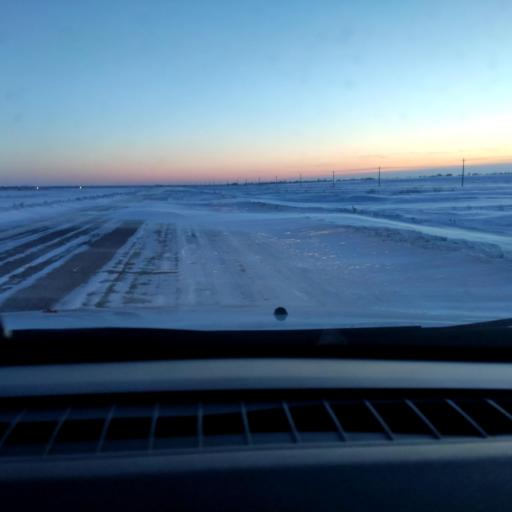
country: RU
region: Samara
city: Georgiyevka
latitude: 53.3624
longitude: 51.0371
